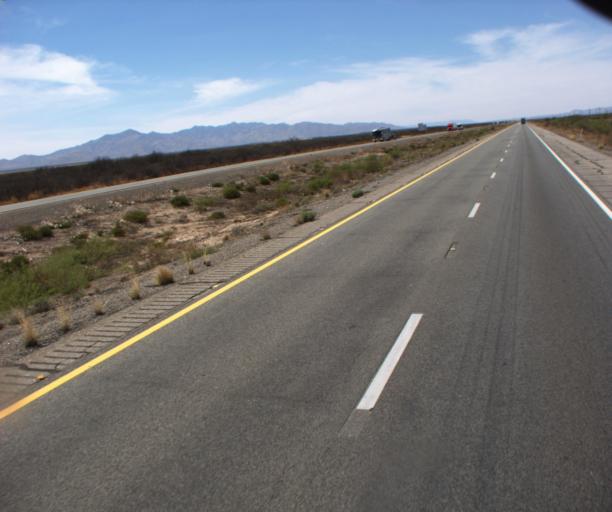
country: US
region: Arizona
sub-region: Cochise County
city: Willcox
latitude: 32.2787
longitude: -109.2721
